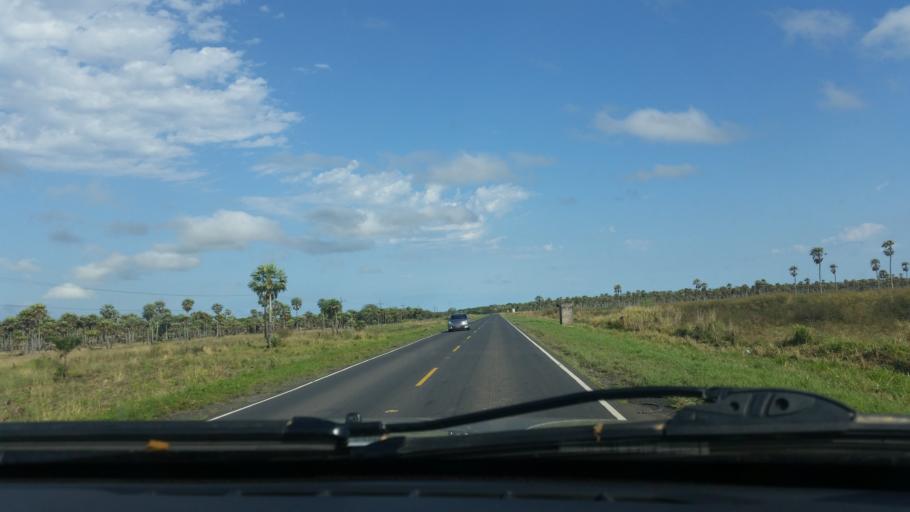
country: PY
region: Presidente Hayes
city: Benjamin Aceval
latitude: -24.9119
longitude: -57.6264
